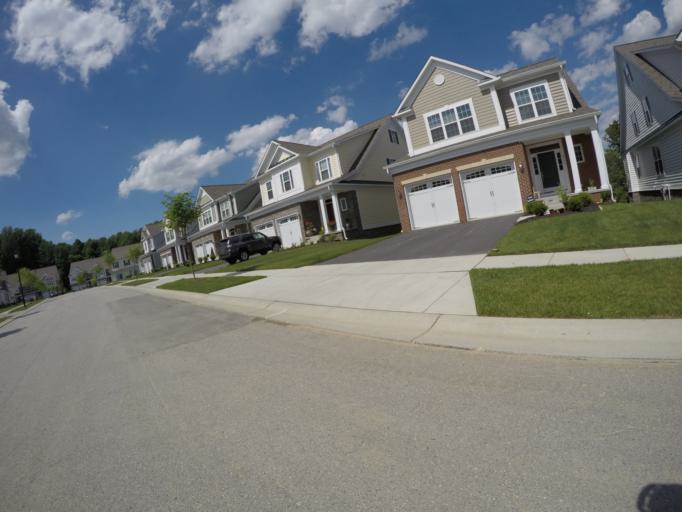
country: US
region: Maryland
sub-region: Howard County
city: Columbia
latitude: 39.3010
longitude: -76.8920
